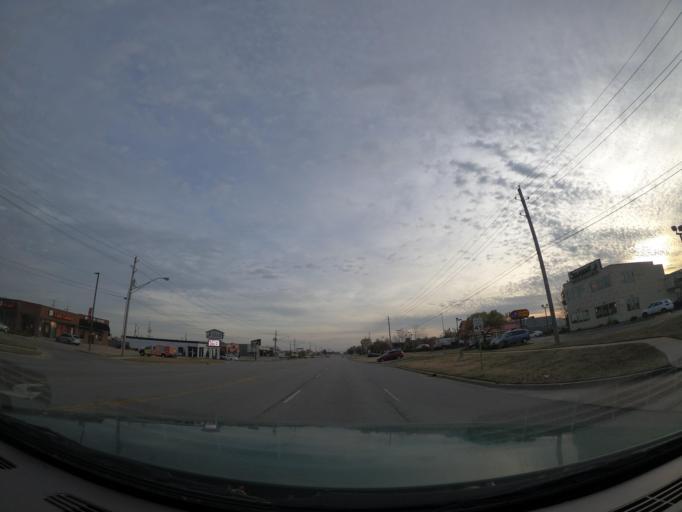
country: US
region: Oklahoma
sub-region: Tulsa County
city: Broken Arrow
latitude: 36.0596
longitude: -95.8154
